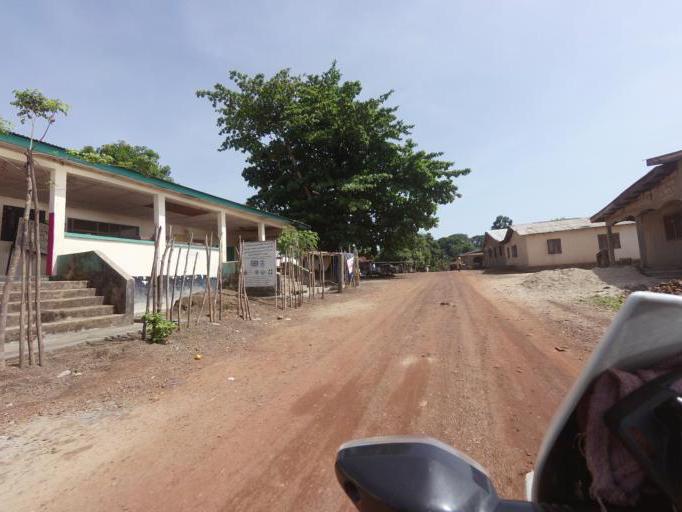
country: SL
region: Northern Province
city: Binkolo
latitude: 9.1075
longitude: -12.2073
